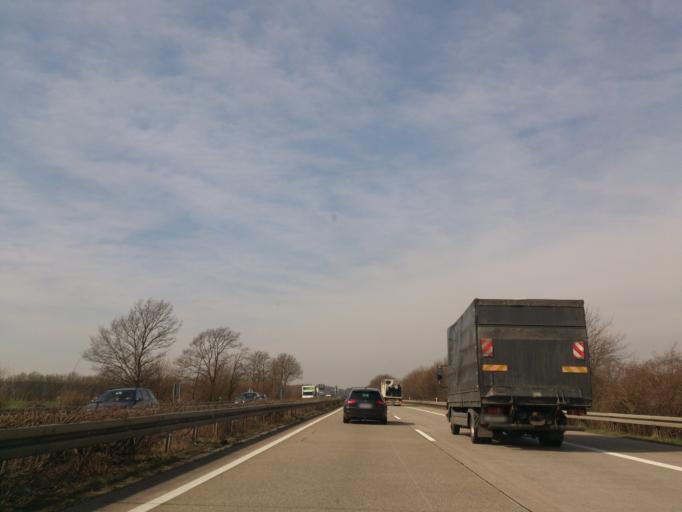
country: DE
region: North Rhine-Westphalia
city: Geseke
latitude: 51.5961
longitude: 8.4996
